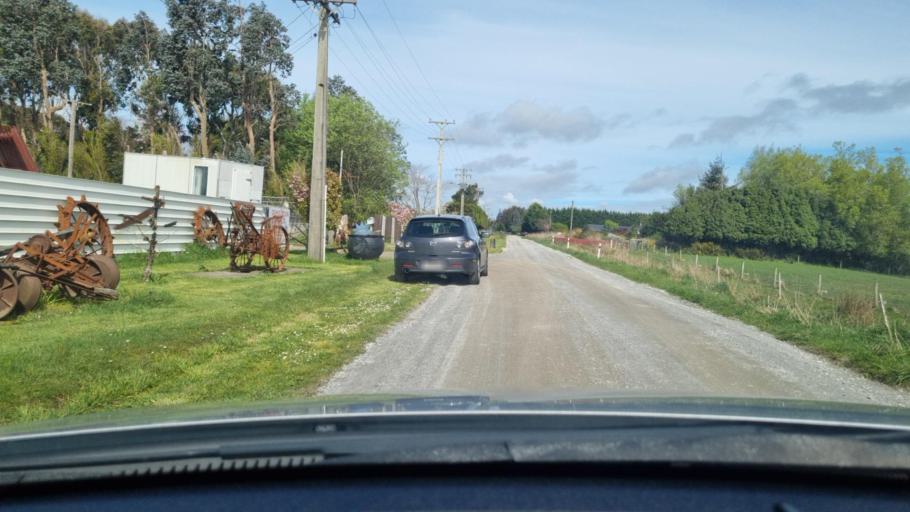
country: NZ
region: Southland
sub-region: Invercargill City
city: Invercargill
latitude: -46.4520
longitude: 168.3776
